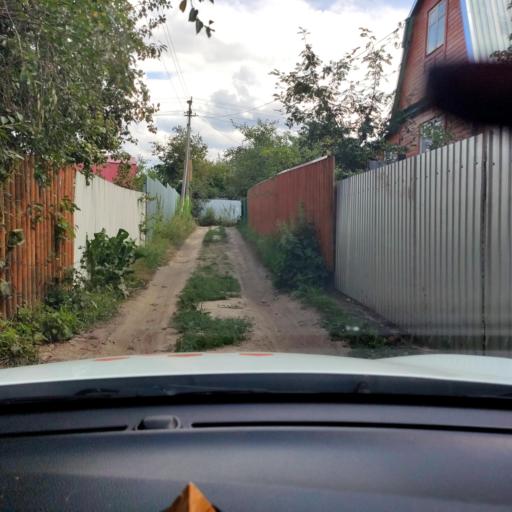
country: RU
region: Tatarstan
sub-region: Zelenodol'skiy Rayon
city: Vasil'yevo
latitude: 55.8298
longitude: 48.7445
